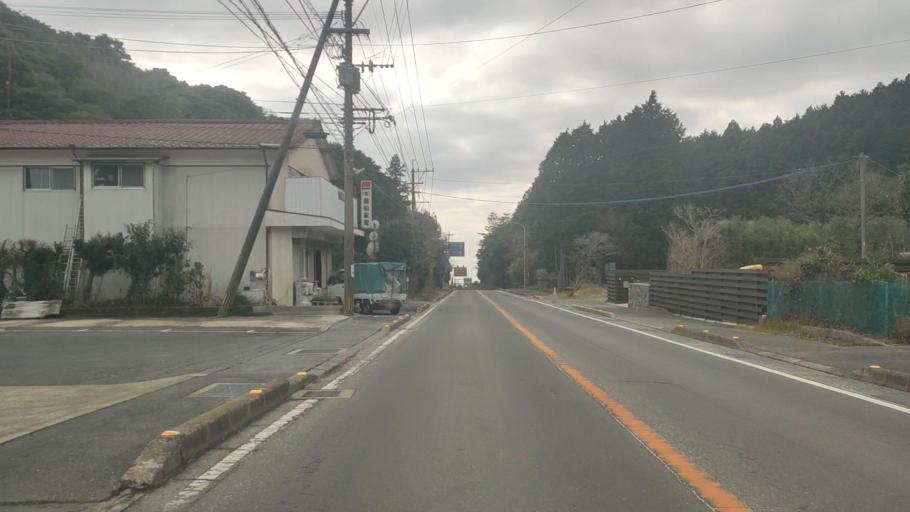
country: JP
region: Nagasaki
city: Shimabara
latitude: 32.7261
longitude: 130.2524
